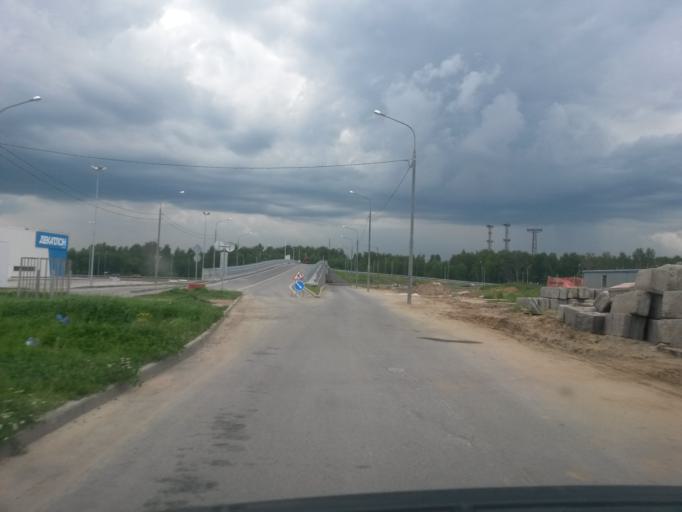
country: RU
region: Moskovskaya
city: Noginsk
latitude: 55.8324
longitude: 38.3709
